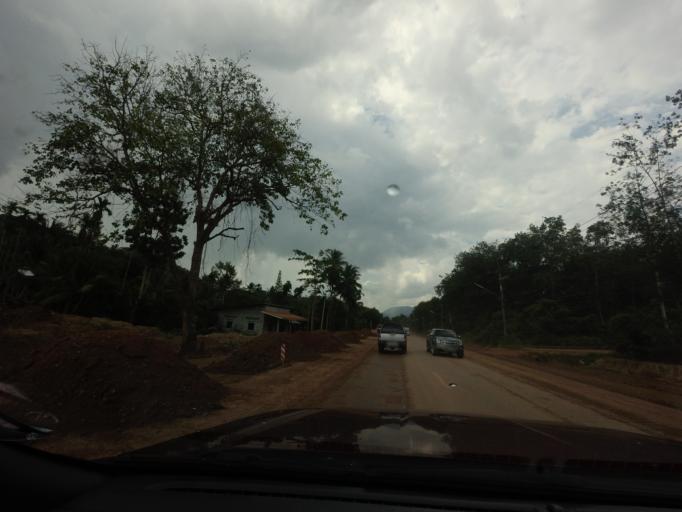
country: TH
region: Yala
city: Ban Nang Sata
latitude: 6.3226
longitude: 101.3037
